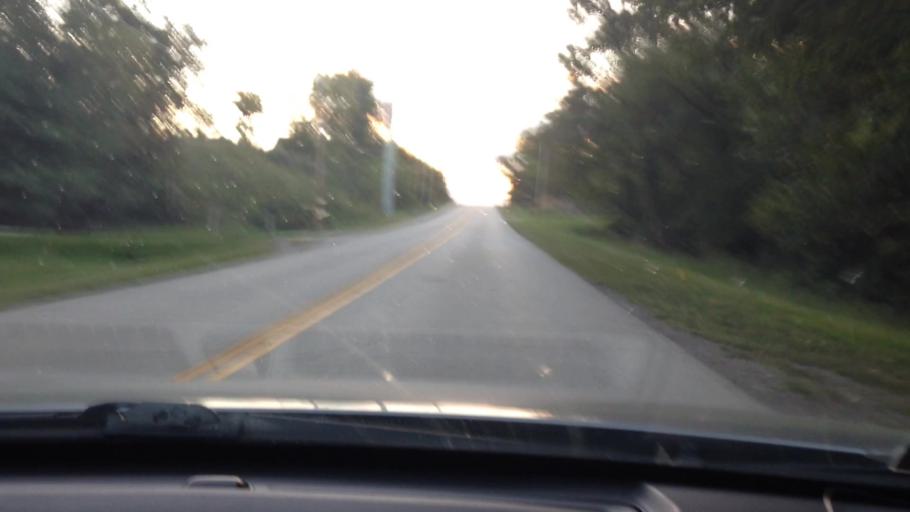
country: US
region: Kansas
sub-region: Leavenworth County
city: Lansing
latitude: 39.1866
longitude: -94.8116
